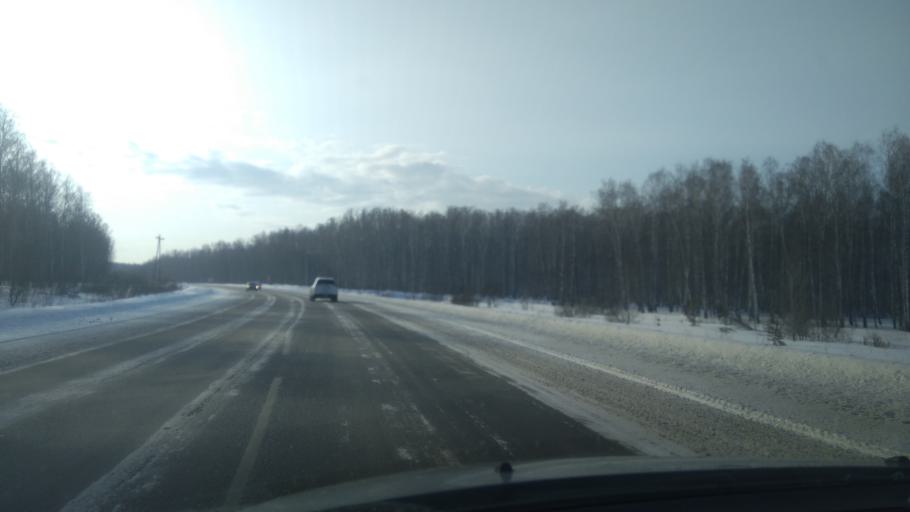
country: RU
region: Sverdlovsk
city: Bogdanovich
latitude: 56.7956
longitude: 62.0039
